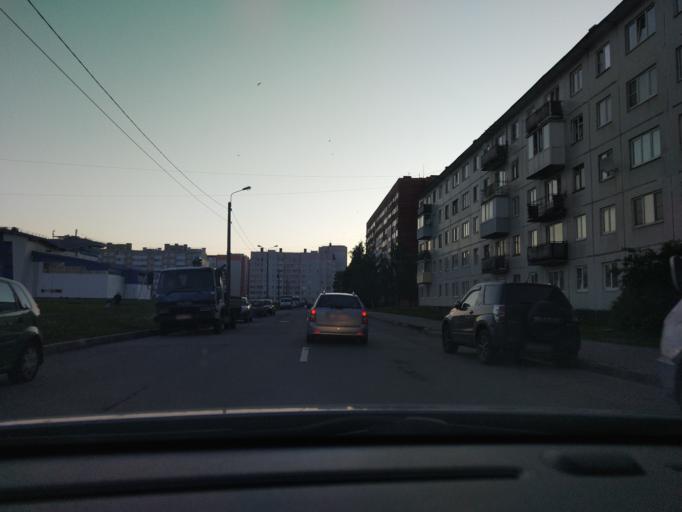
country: RU
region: St.-Petersburg
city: Krasnoye Selo
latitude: 59.7428
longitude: 30.0896
